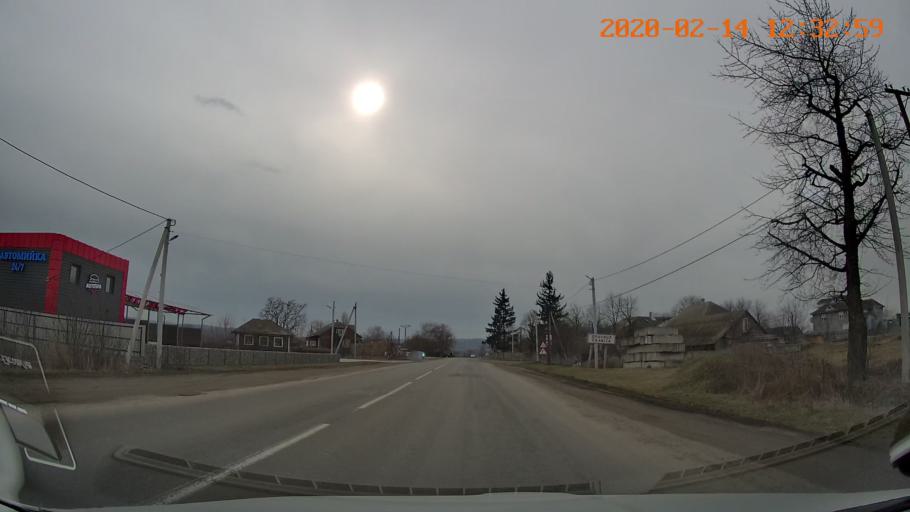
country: RO
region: Botosani
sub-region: Comuna Darabani
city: Bajura
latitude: 48.2373
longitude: 26.5468
